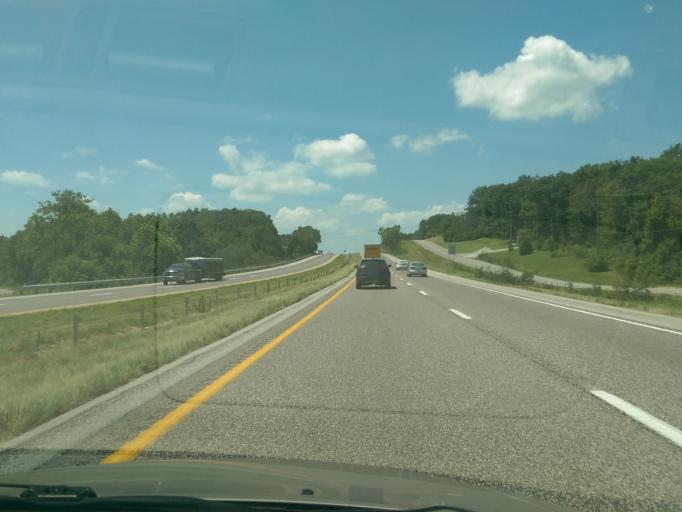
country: US
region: Missouri
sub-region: Boone County
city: Columbia
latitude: 38.9696
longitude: -92.3816
